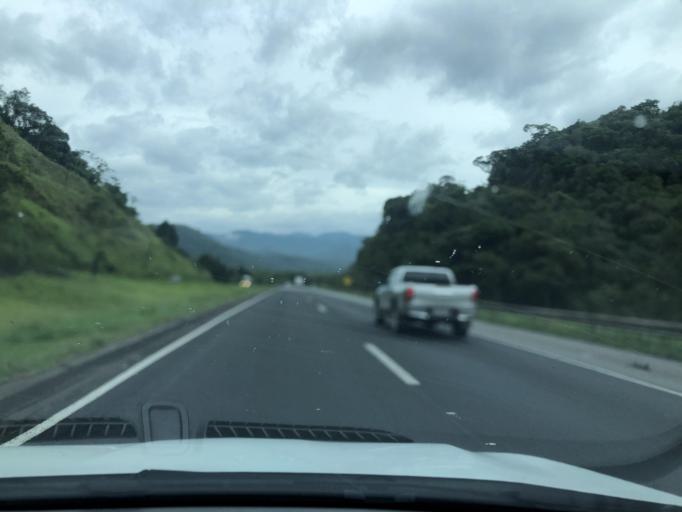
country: BR
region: Sao Paulo
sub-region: Miracatu
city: Miracatu
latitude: -24.2289
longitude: -47.3617
